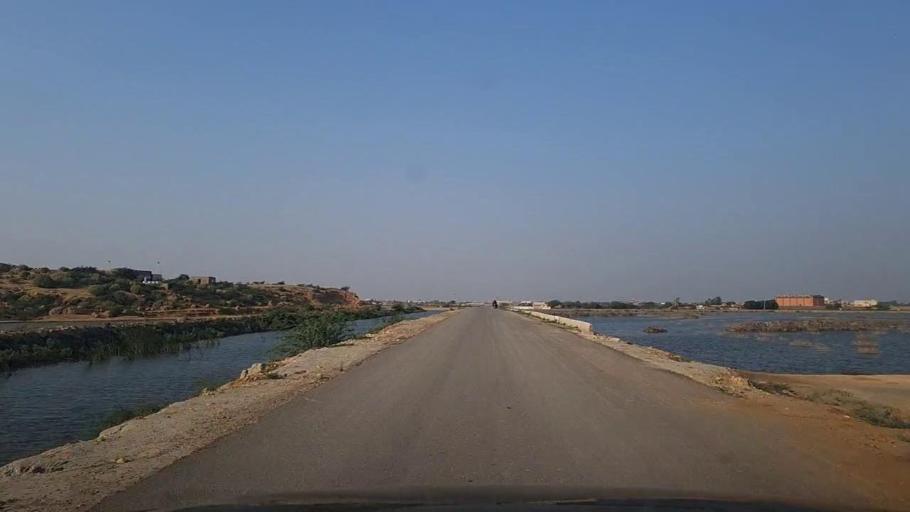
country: PK
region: Sindh
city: Thatta
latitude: 24.7418
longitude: 67.9067
